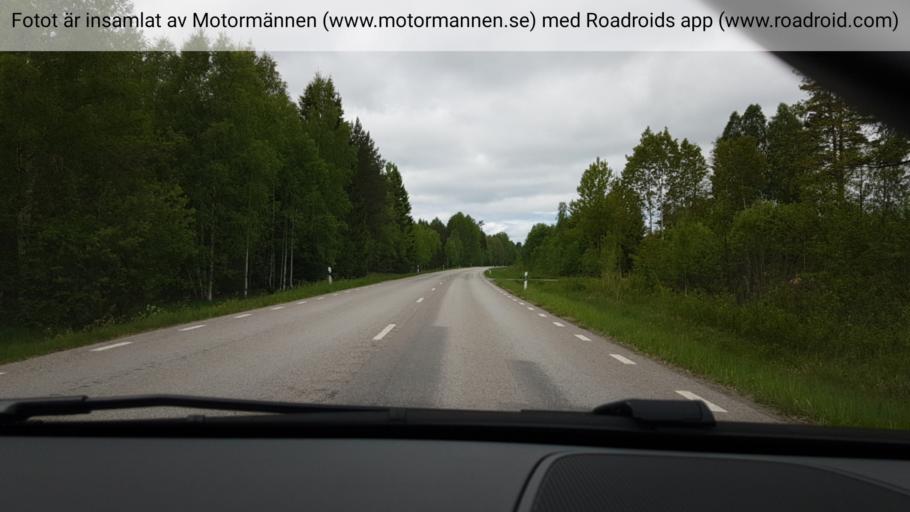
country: SE
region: Uppsala
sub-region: Heby Kommun
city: OEstervala
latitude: 60.3664
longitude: 17.2870
